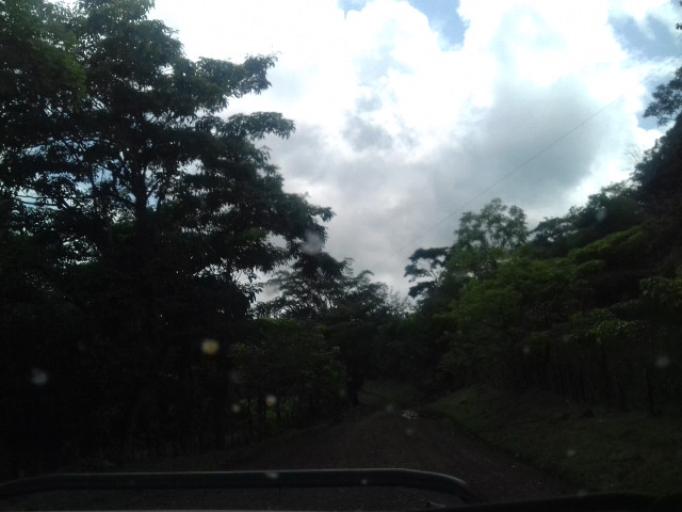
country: NI
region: Matagalpa
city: Matiguas
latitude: 12.8992
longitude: -85.3656
